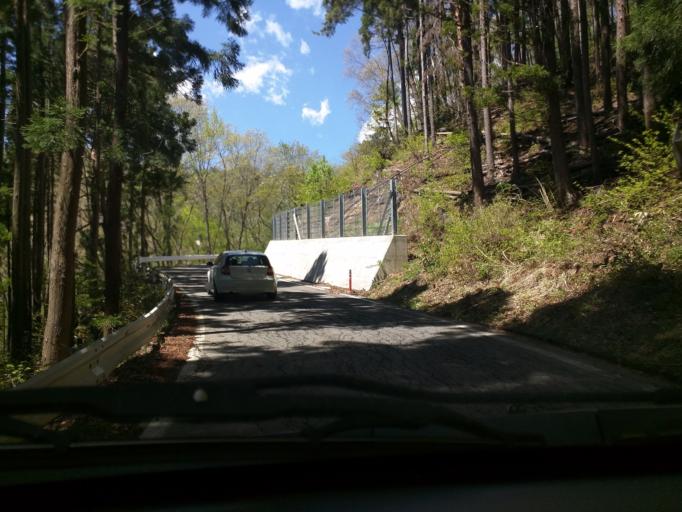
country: JP
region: Nagano
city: Nagano-shi
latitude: 36.6889
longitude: 138.1105
